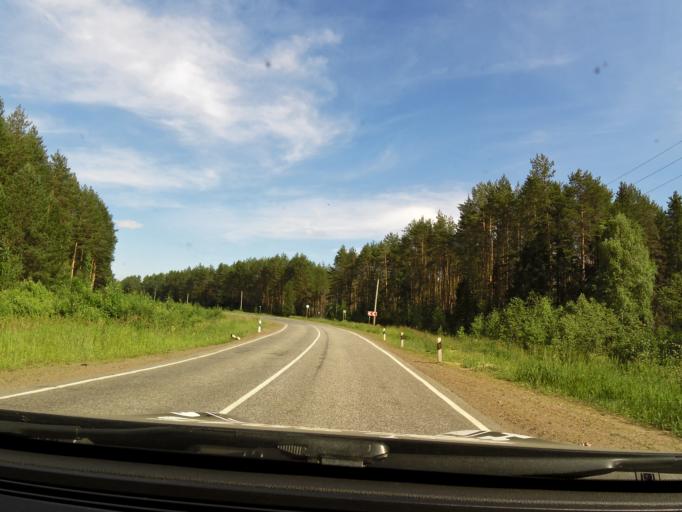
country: RU
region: Kirov
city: Belaya Kholunitsa
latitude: 58.8406
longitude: 50.7793
